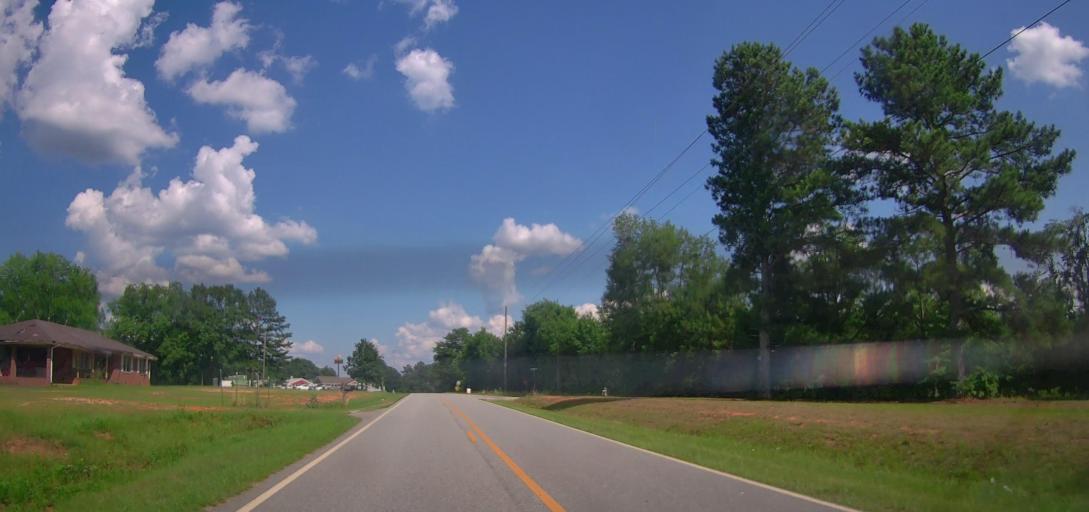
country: US
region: Georgia
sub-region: Butts County
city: Jackson
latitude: 33.2114
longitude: -84.0667
